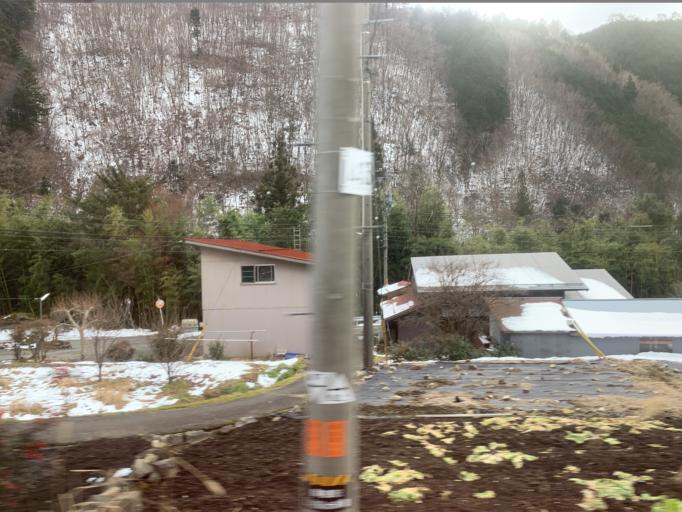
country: JP
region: Gifu
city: Takayama
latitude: 35.9966
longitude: 137.2834
